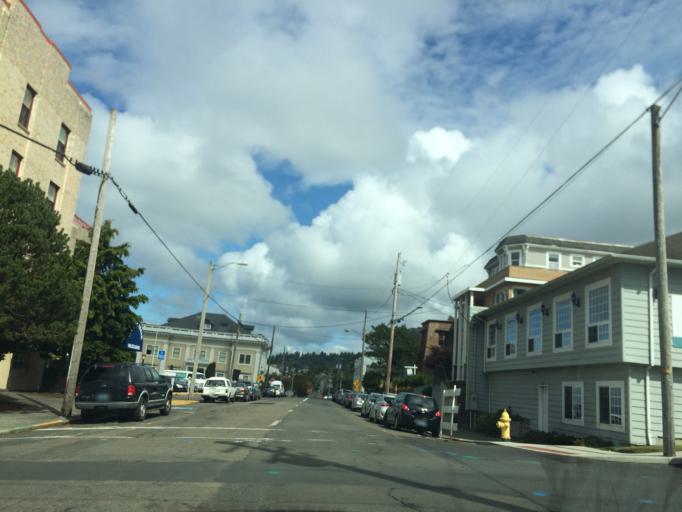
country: US
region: Oregon
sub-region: Clatsop County
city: Astoria
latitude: 46.1880
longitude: -123.8273
